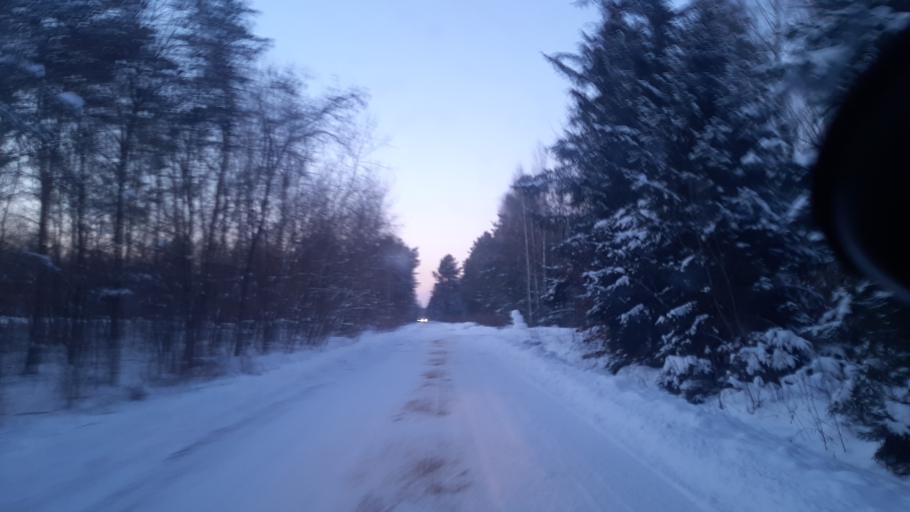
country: PL
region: Lublin Voivodeship
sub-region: Powiat lubelski
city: Jastkow
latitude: 51.3710
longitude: 22.5228
